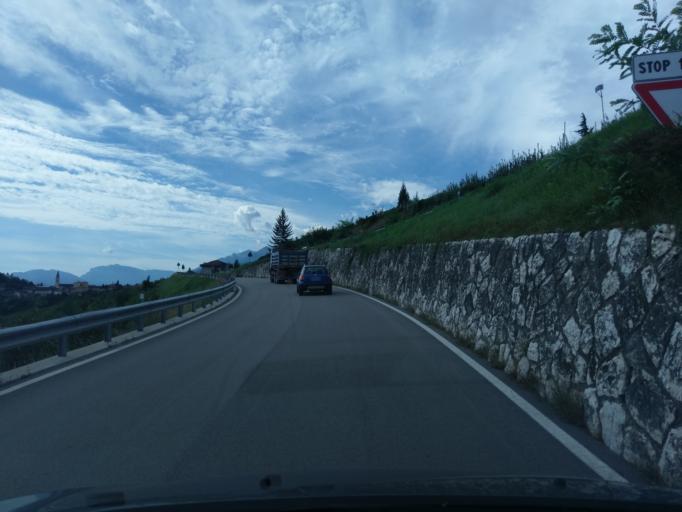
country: IT
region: Trentino-Alto Adige
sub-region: Provincia di Trento
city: Cles
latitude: 46.3766
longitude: 11.0345
